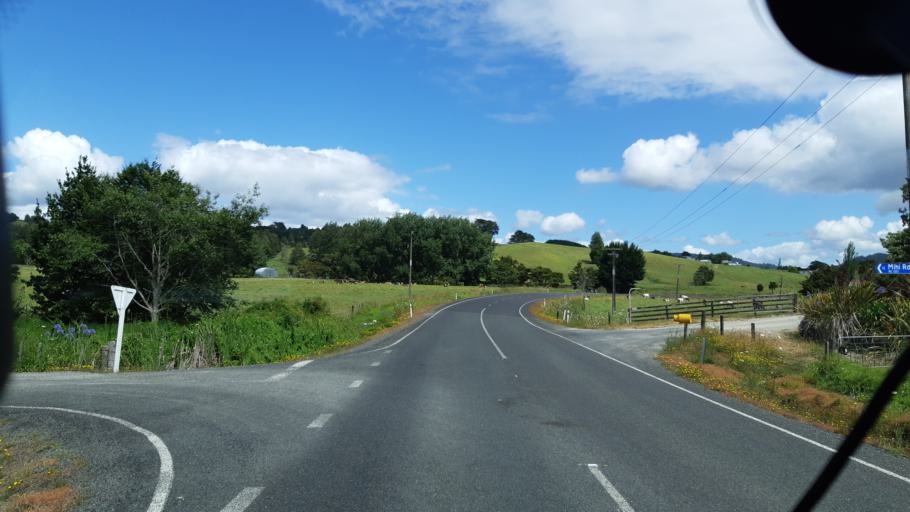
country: NZ
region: Northland
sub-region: Far North District
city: Waimate North
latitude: -35.3028
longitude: 173.7410
